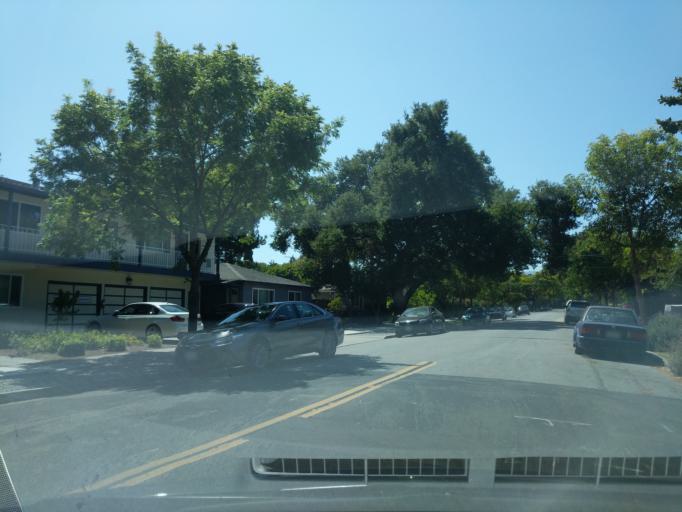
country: US
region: California
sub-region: Santa Clara County
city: Mountain View
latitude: 37.3925
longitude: -122.0841
